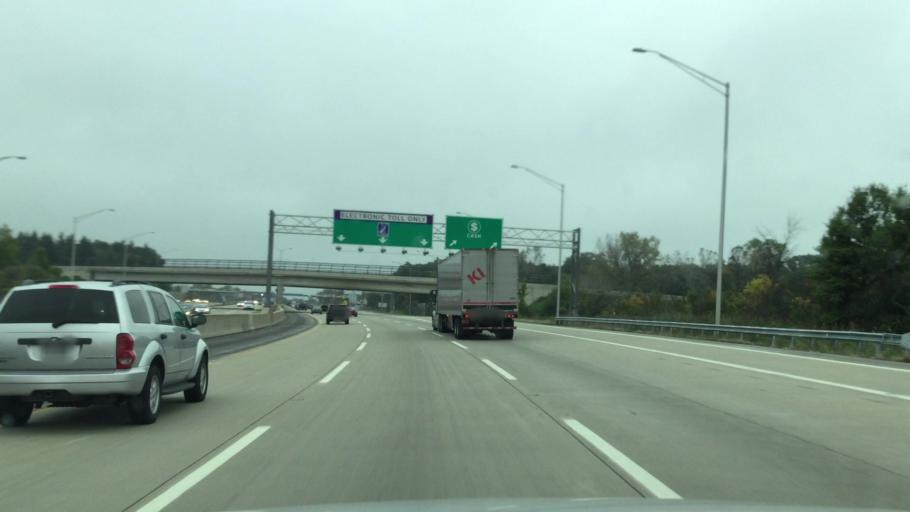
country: US
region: Illinois
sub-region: Lake County
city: Wadsworth
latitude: 42.4275
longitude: -87.9482
